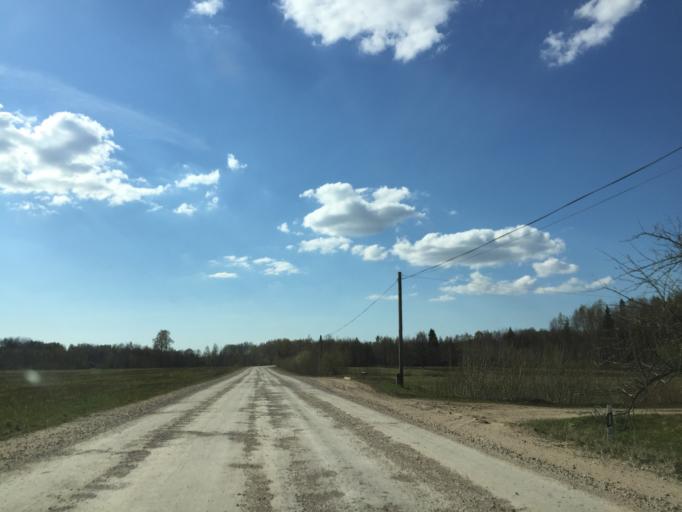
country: LV
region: Seja
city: Loja
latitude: 57.3439
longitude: 24.6014
